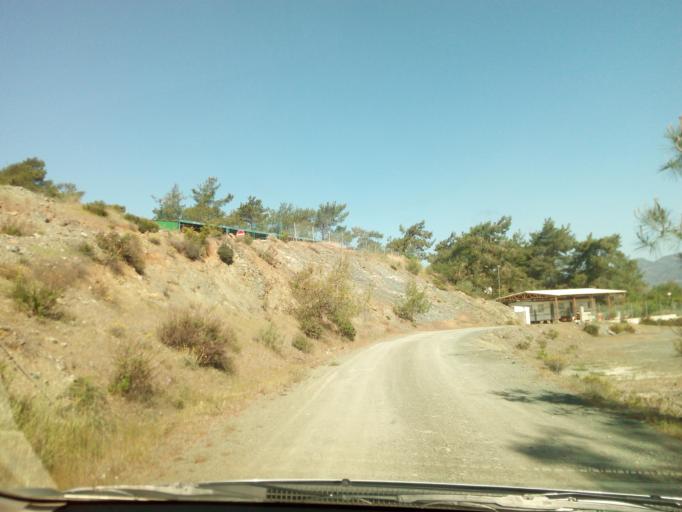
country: CY
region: Limassol
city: Pelendri
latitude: 34.8290
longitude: 33.0499
